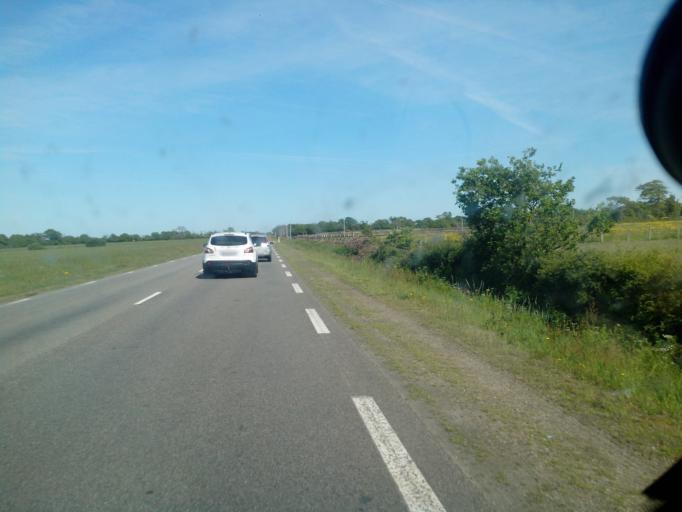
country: FR
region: Pays de la Loire
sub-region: Departement de la Loire-Atlantique
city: La Bernerie-en-Retz
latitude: 47.1117
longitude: -2.0124
